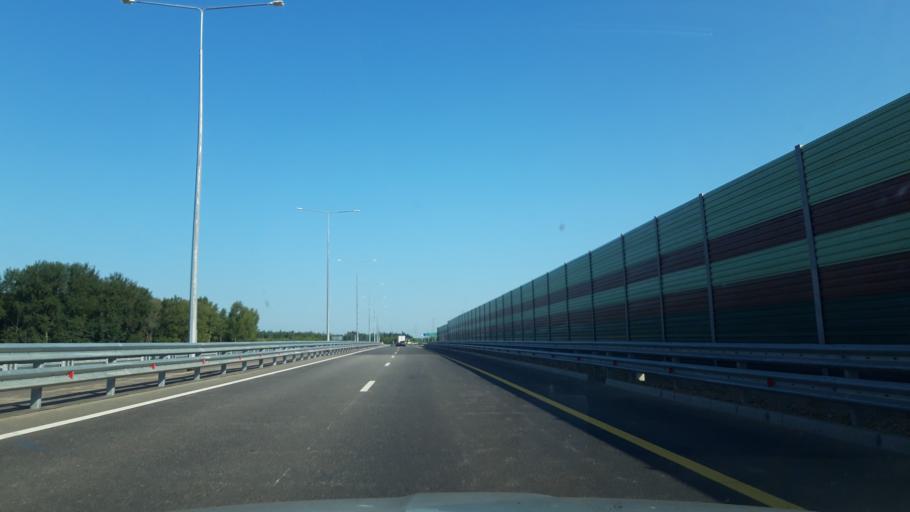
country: RU
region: Moskovskaya
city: Spas-Zaulok
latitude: 56.4916
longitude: 36.5318
